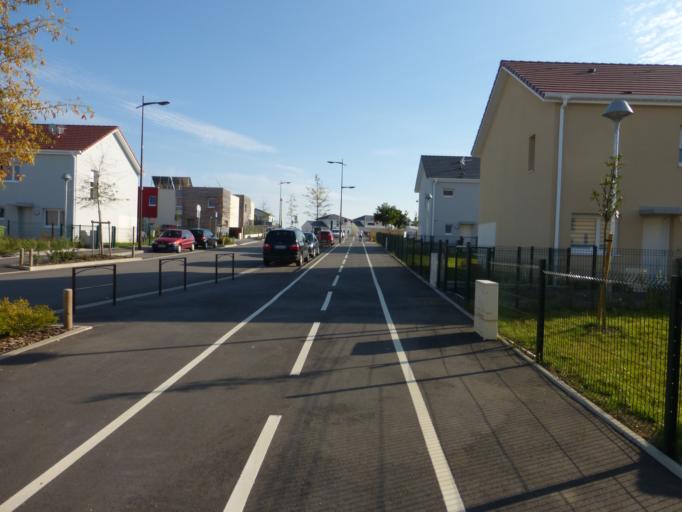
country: FR
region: Lorraine
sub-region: Departement de Meurthe-et-Moselle
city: Pulnoy
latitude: 48.7004
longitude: 6.2509
